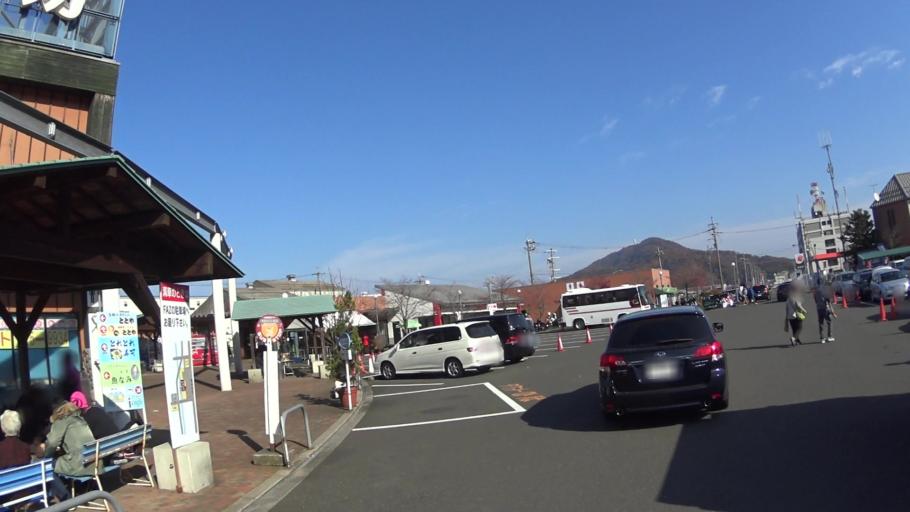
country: JP
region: Kyoto
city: Maizuru
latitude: 35.4502
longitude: 135.3149
